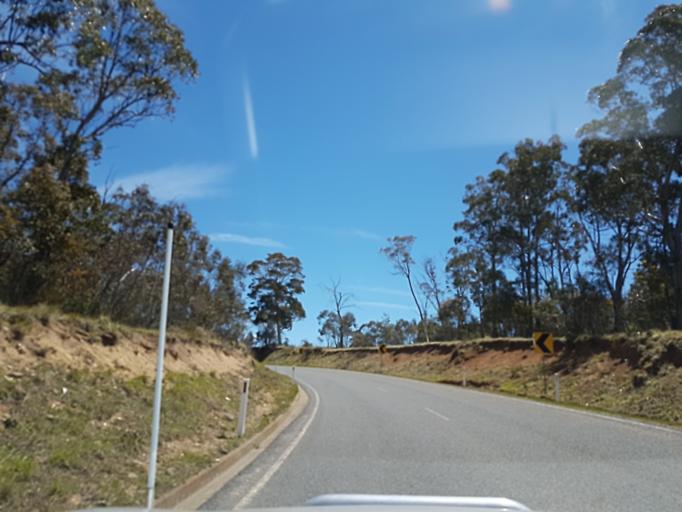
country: AU
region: Victoria
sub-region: Alpine
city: Mount Beauty
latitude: -37.0815
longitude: 147.3891
